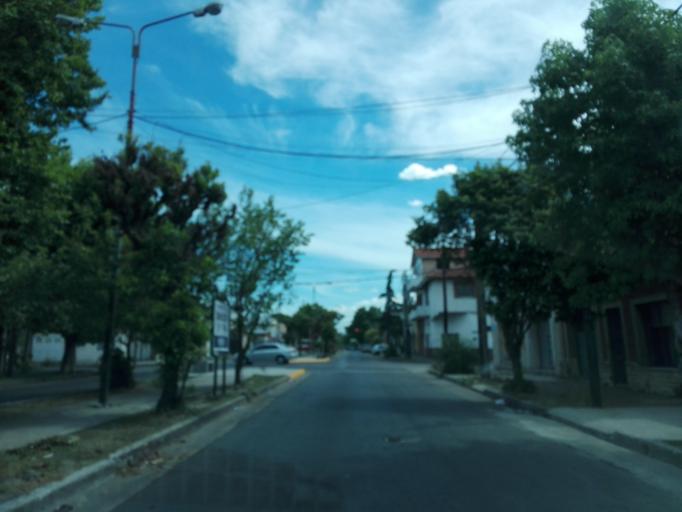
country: AR
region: Buenos Aires
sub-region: Partido de Lanus
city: Lanus
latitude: -34.7128
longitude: -58.3788
